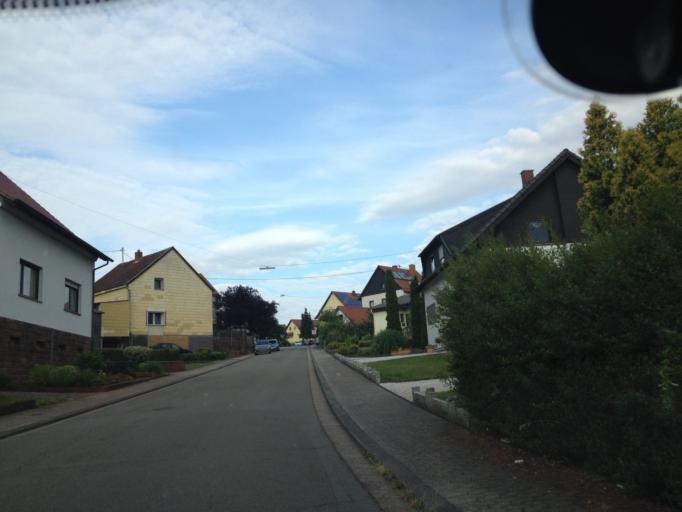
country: DE
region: Saarland
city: Illingen
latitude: 49.3817
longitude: 7.0790
